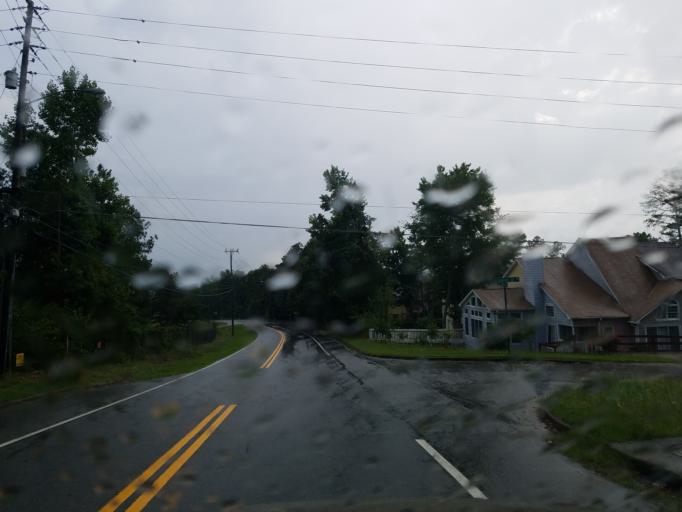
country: US
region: Georgia
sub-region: Cobb County
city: Marietta
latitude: 33.9724
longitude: -84.5033
